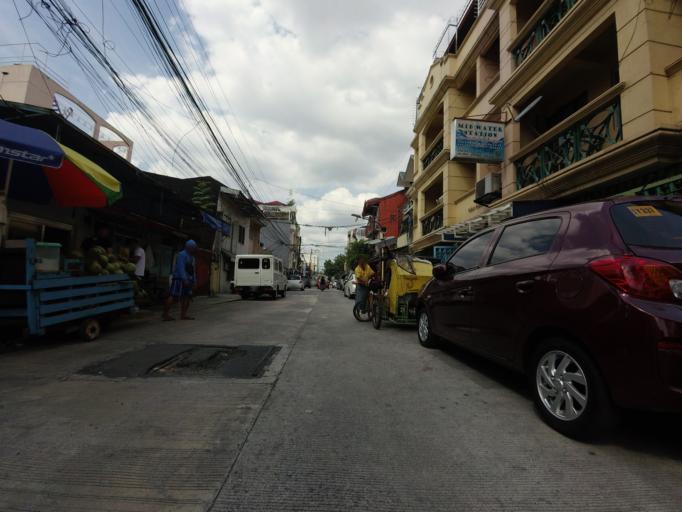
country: PH
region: Metro Manila
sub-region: Makati City
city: Makati City
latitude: 14.5701
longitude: 121.0038
